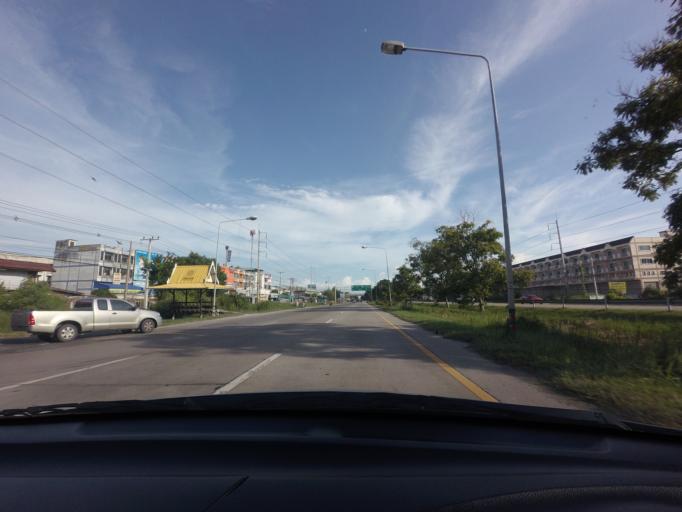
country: TH
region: Phra Nakhon Si Ayutthaya
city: Lat Bua Luang
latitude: 14.1653
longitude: 100.2913
